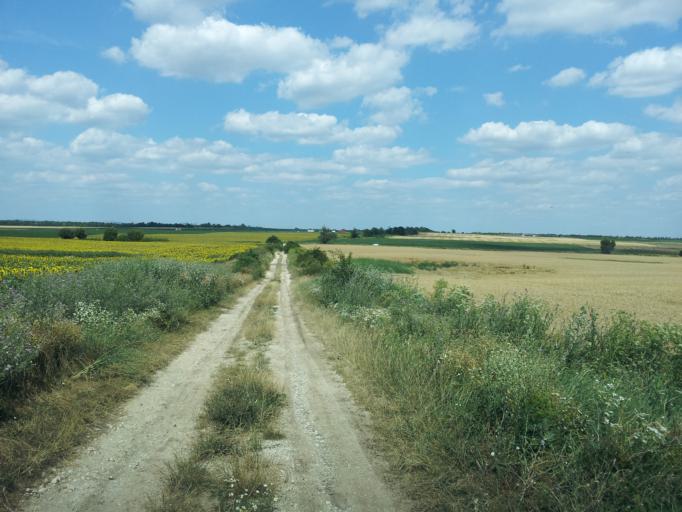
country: HU
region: Veszprem
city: Balatonkenese
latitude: 47.0557
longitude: 18.0799
